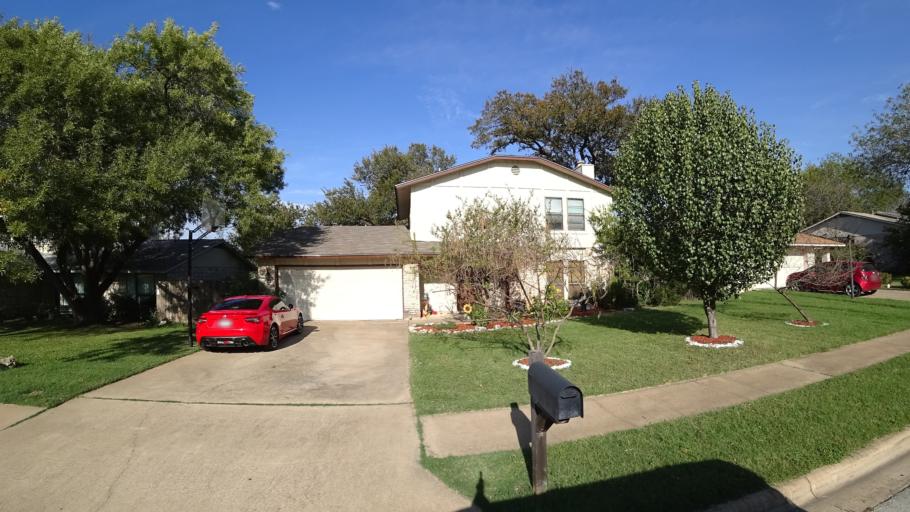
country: US
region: Texas
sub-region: Williamson County
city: Anderson Mill
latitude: 30.4523
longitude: -97.8086
